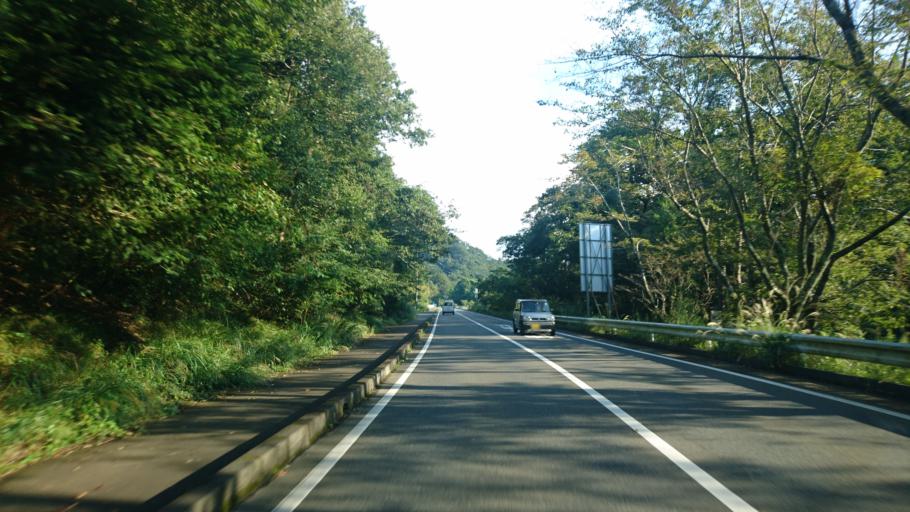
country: JP
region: Chiba
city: Kawaguchi
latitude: 35.1774
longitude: 140.0074
